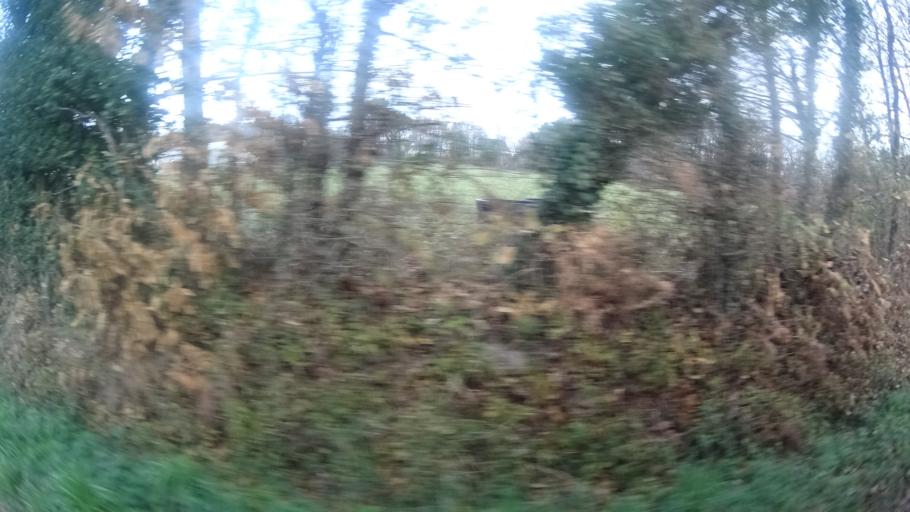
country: FR
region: Pays de la Loire
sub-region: Departement de la Loire-Atlantique
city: Saint-Nicolas-de-Redon
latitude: 47.6397
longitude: -2.0422
